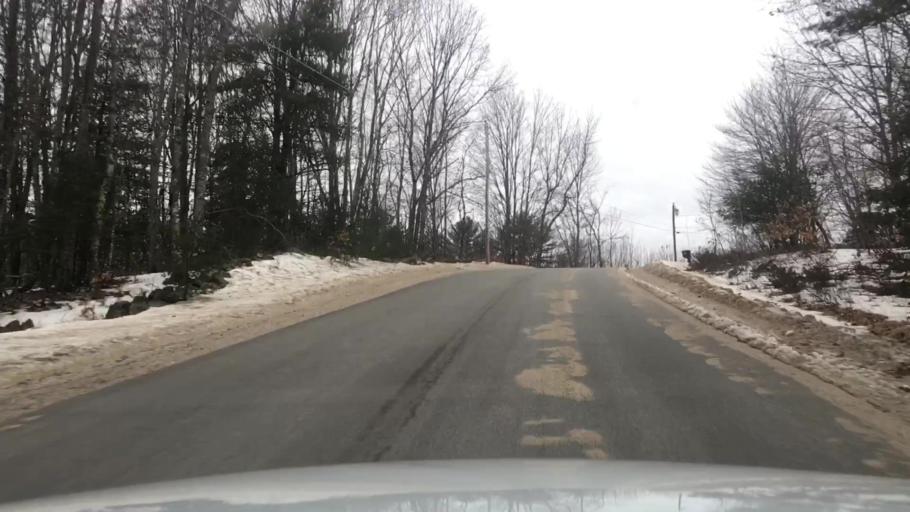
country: US
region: Maine
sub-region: York County
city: Springvale
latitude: 43.4974
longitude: -70.8167
